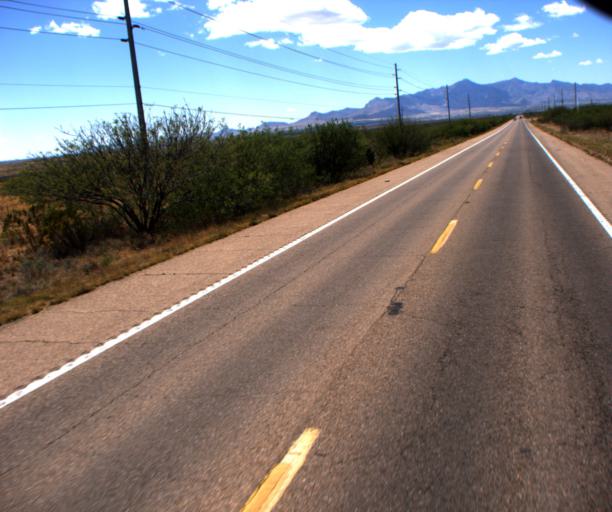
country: US
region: Arizona
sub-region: Cochise County
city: Naco
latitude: 31.3748
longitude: -109.9990
